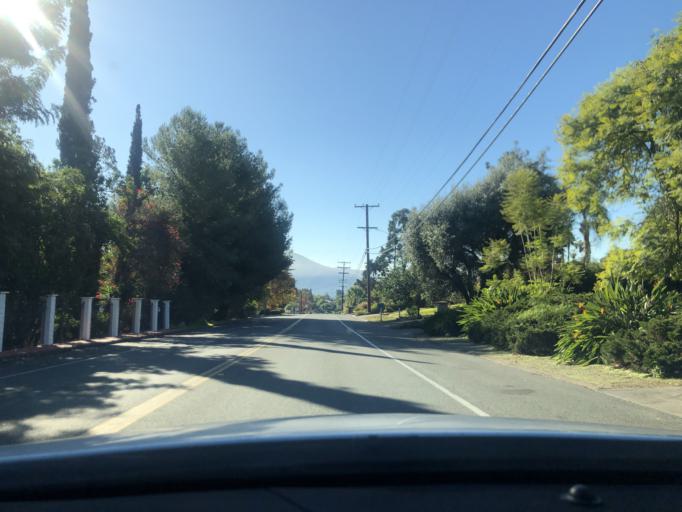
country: US
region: California
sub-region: San Diego County
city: Rancho San Diego
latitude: 32.7687
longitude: -116.9410
